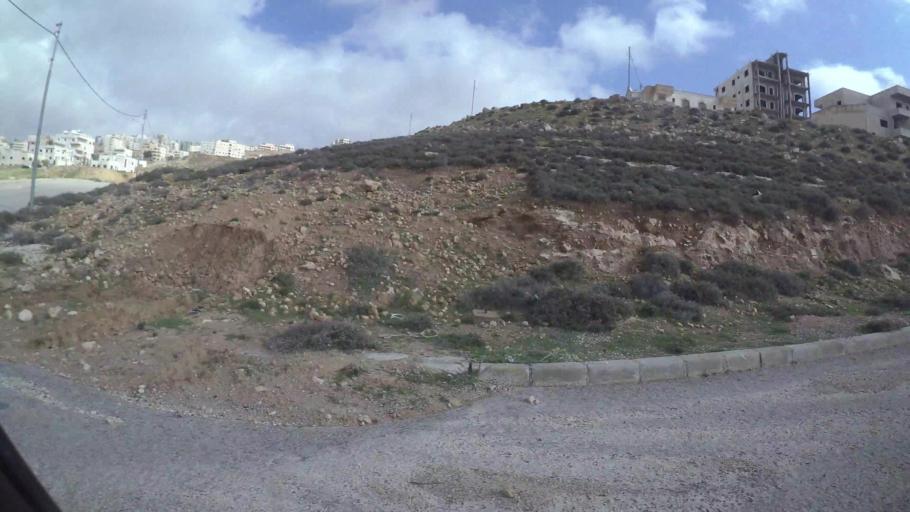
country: JO
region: Amman
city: Al Jubayhah
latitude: 32.0592
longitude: 35.8612
